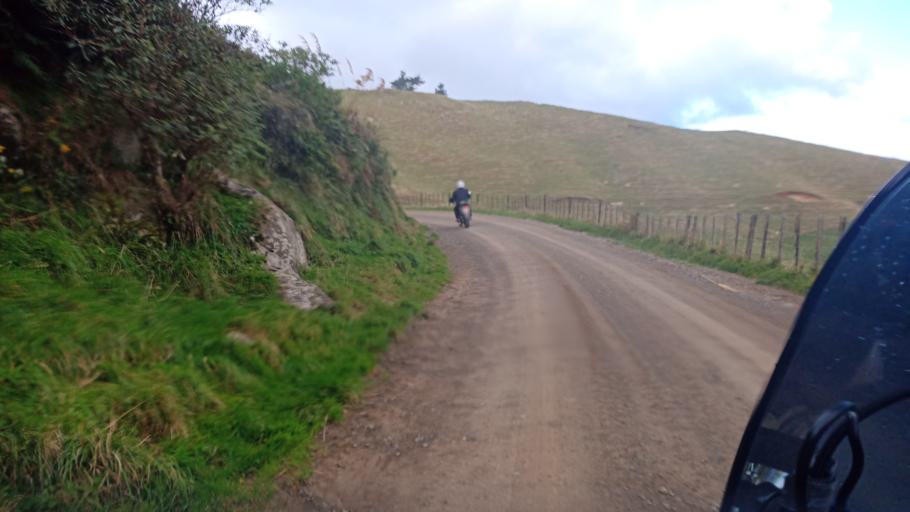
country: NZ
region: Gisborne
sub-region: Gisborne District
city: Gisborne
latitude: -38.4846
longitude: 177.6057
